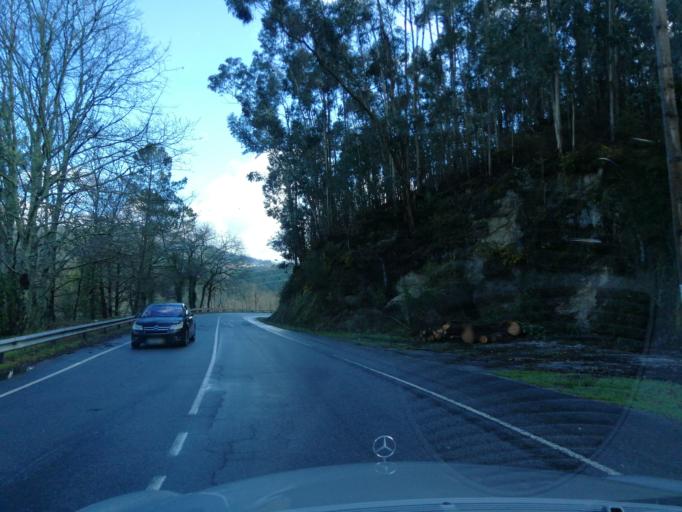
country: PT
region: Viana do Castelo
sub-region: Ponte da Barca
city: Ponte da Barca
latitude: 41.8093
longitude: -8.3776
